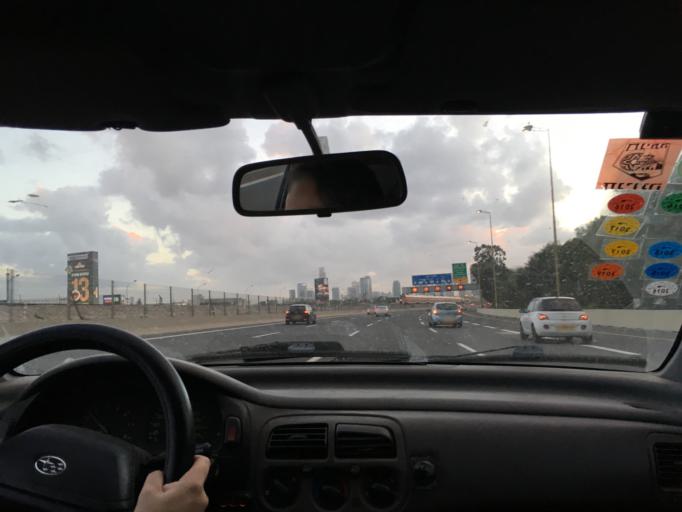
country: IL
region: Tel Aviv
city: Ramat Gan
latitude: 32.1128
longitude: 34.8100
